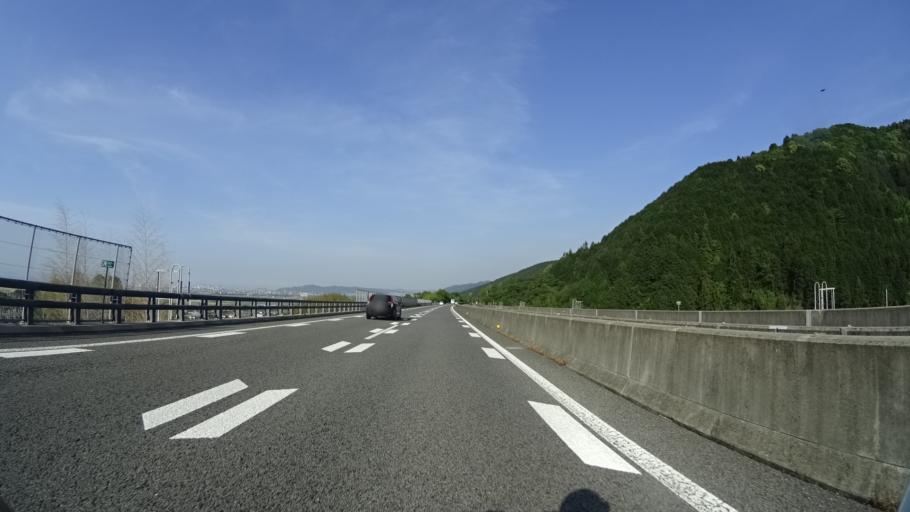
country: JP
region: Ehime
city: Saijo
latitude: 33.8846
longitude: 133.1326
